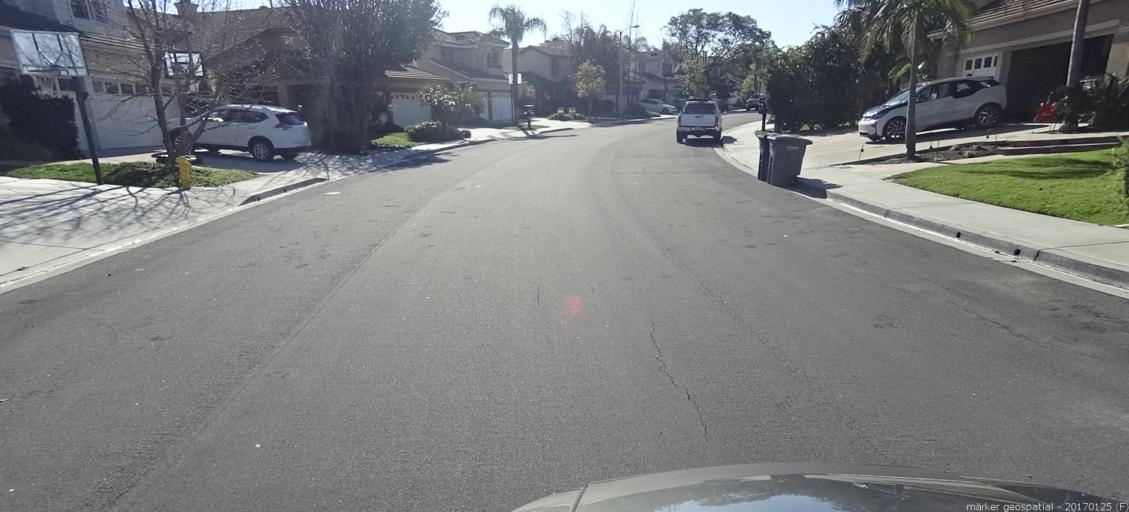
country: US
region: California
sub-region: Orange County
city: Portola Hills
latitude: 33.6766
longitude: -117.6283
